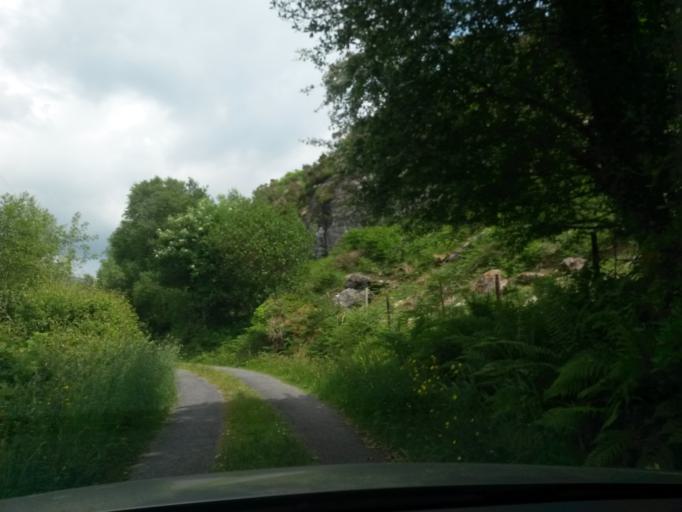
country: IE
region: Munster
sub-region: Ciarrai
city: Kenmare
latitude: 51.8141
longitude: -9.5263
